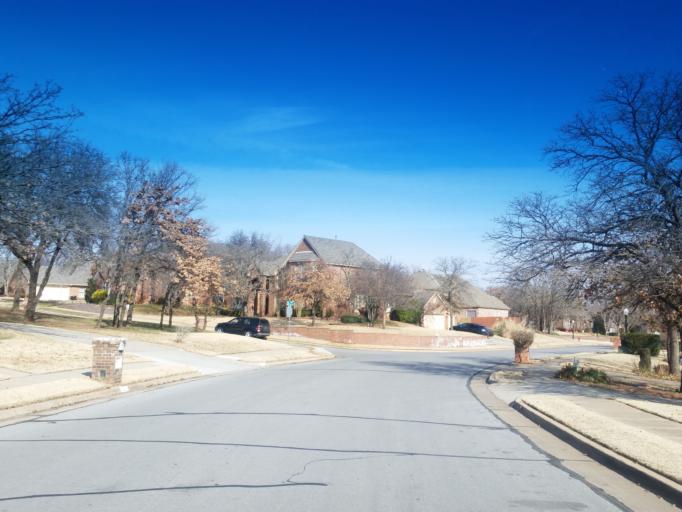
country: US
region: Oklahoma
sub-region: Oklahoma County
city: Edmond
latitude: 35.6446
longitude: -97.4309
